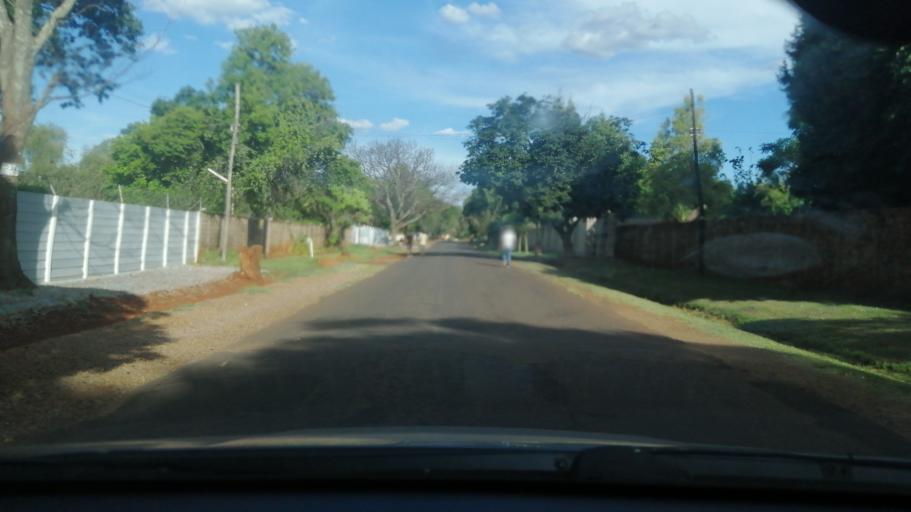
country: ZW
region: Harare
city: Harare
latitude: -17.7645
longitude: 31.0522
